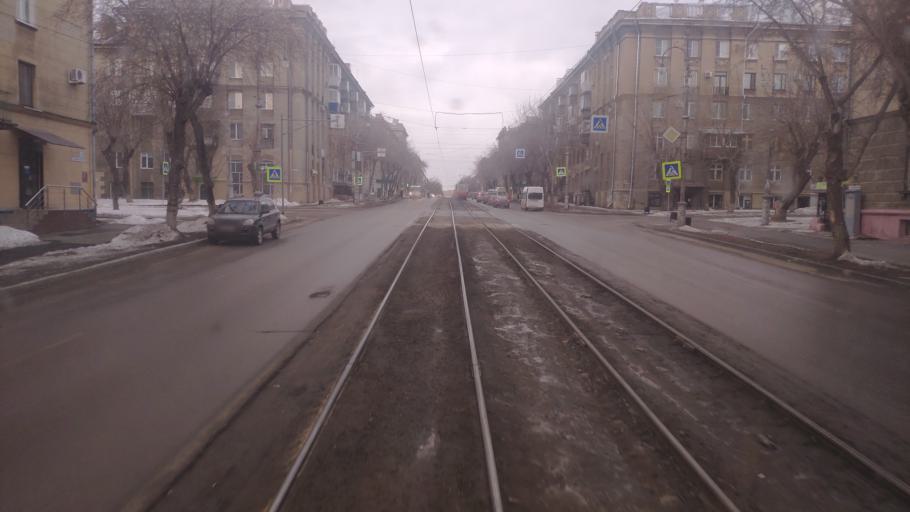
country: RU
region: Chelyabinsk
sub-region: Gorod Magnitogorsk
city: Magnitogorsk
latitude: 53.4198
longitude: 58.9987
